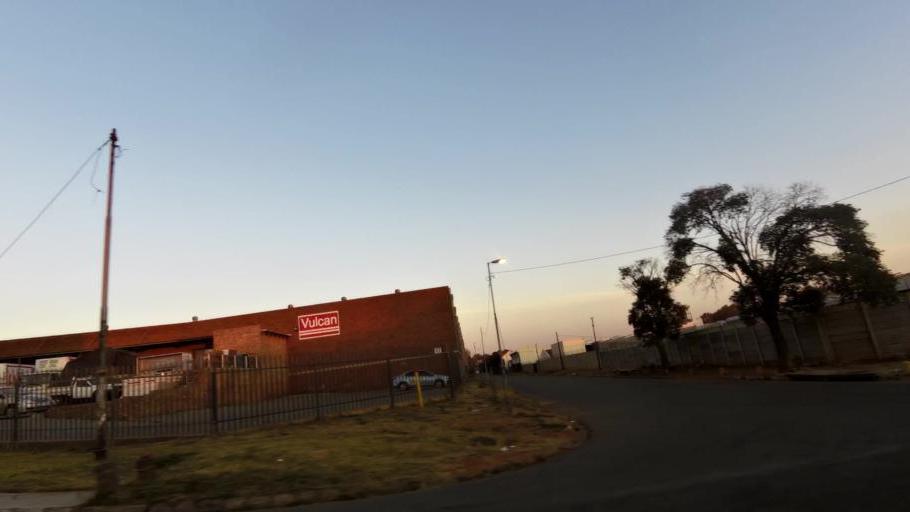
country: ZA
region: Gauteng
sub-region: City of Johannesburg Metropolitan Municipality
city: Johannesburg
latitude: -26.1988
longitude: 27.9780
